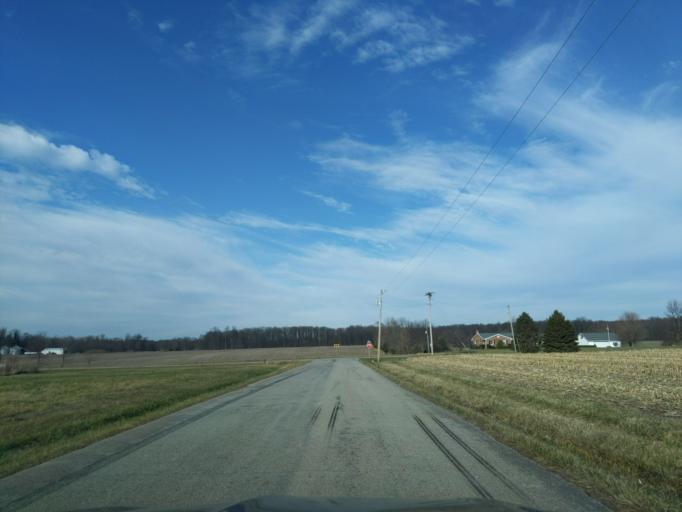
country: US
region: Indiana
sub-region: Decatur County
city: Greensburg
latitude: 39.2628
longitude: -85.4188
